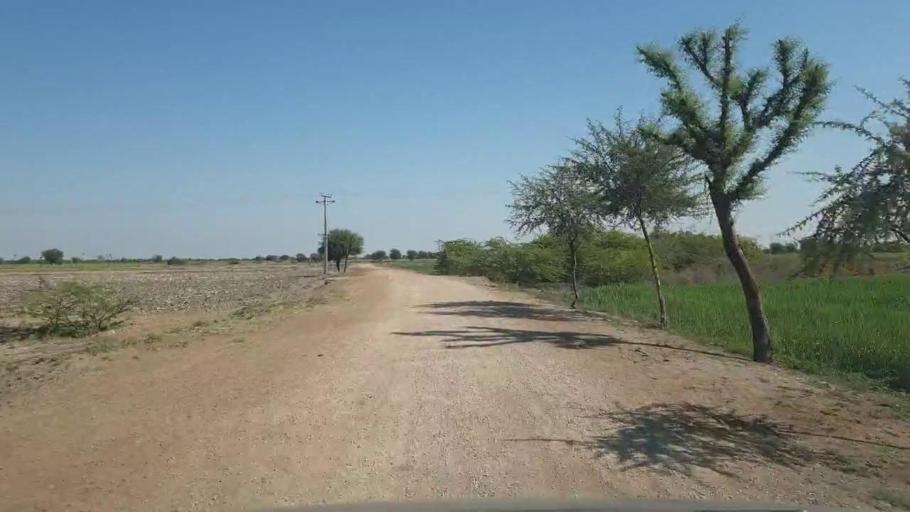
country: PK
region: Sindh
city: Dhoro Naro
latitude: 25.4124
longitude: 69.6221
